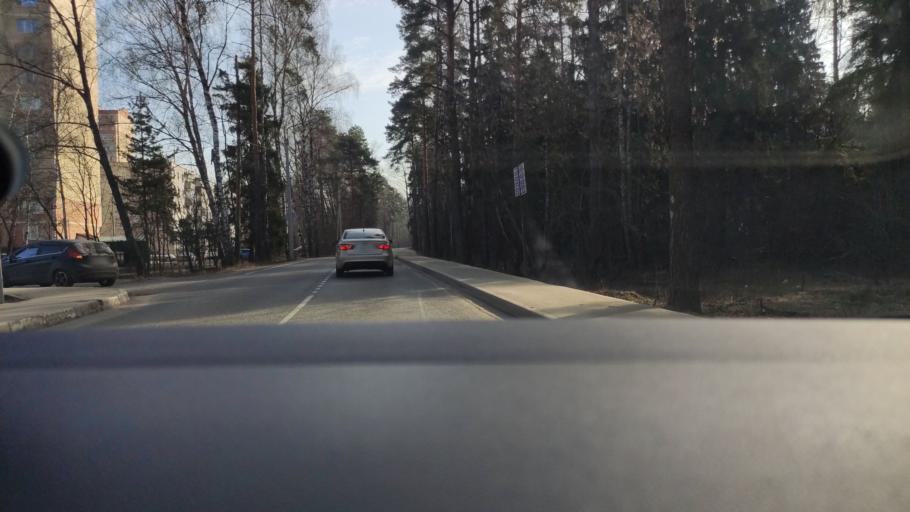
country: RU
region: Moskovskaya
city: Zarya
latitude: 55.8069
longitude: 38.0959
